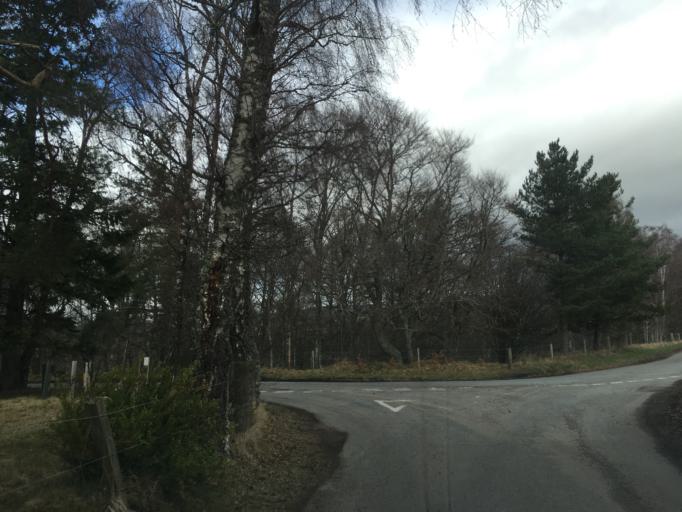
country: GB
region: Scotland
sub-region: Highland
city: Aviemore
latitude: 57.1104
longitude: -3.9238
